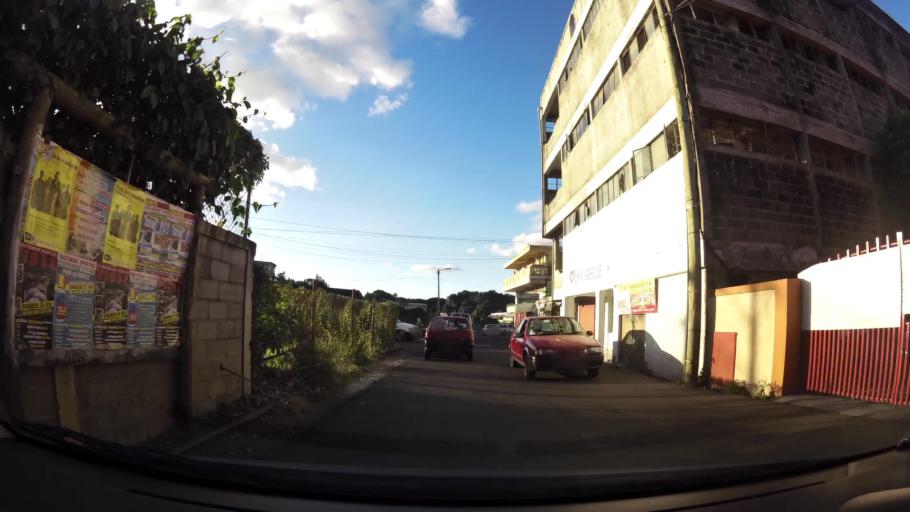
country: MU
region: Plaines Wilhems
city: Quatre Bornes
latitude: -20.2457
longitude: 57.4617
